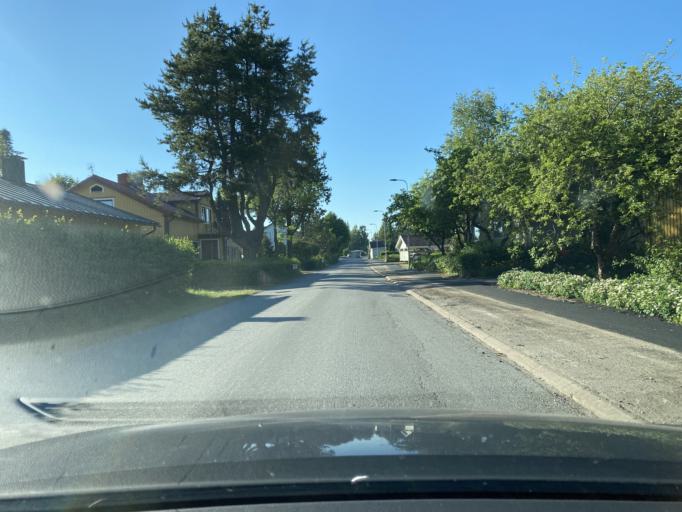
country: FI
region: Satakunta
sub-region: Pori
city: Huittinen
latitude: 61.1725
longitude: 22.6959
